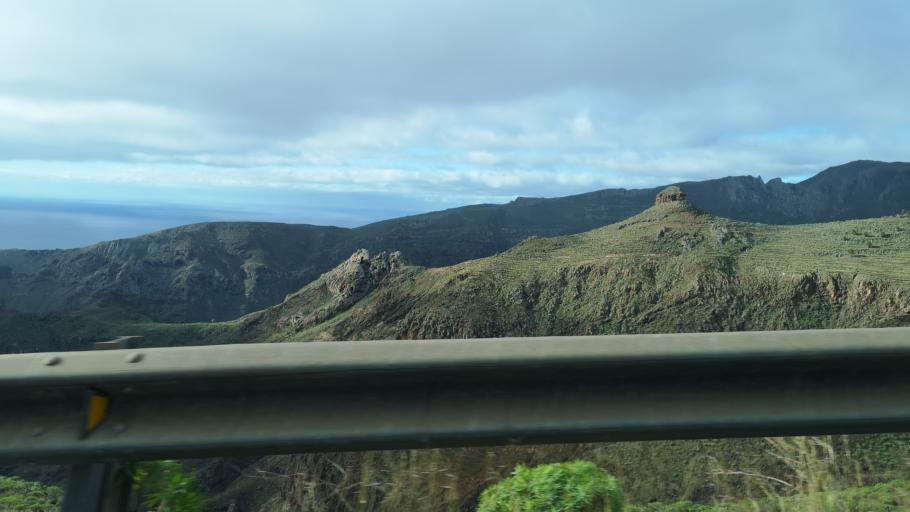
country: ES
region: Canary Islands
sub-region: Provincia de Santa Cruz de Tenerife
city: San Sebastian de la Gomera
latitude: 28.0944
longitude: -17.1542
